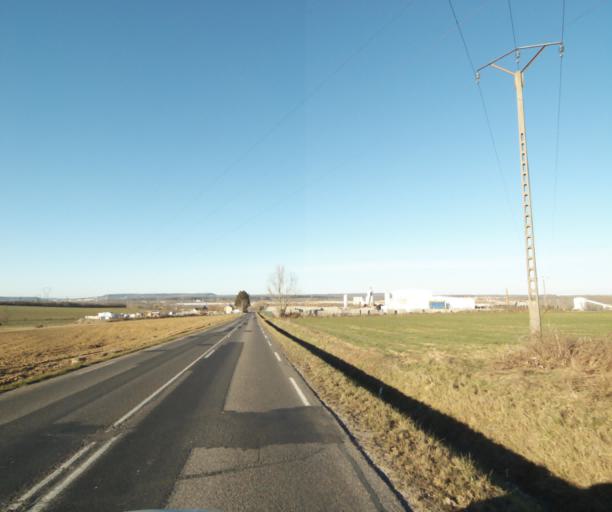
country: FR
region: Lorraine
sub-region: Departement de Meurthe-et-Moselle
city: Art-sur-Meurthe
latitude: 48.6349
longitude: 6.2545
